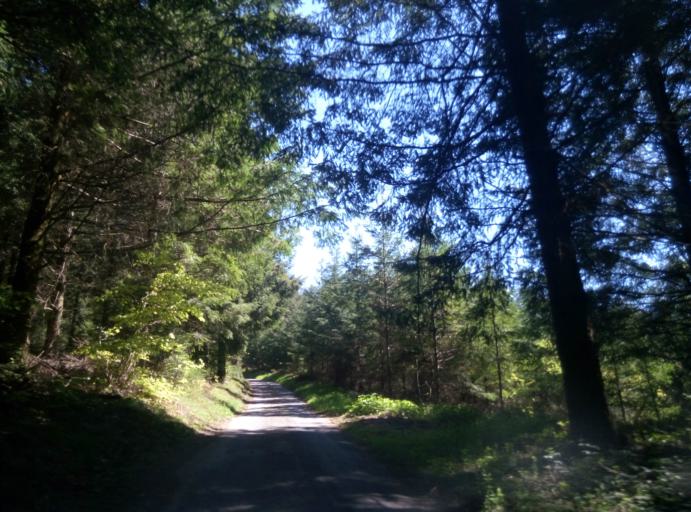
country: FR
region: Rhone-Alpes
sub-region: Departement du Rhone
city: Cublize
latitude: 46.0094
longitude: 4.4210
